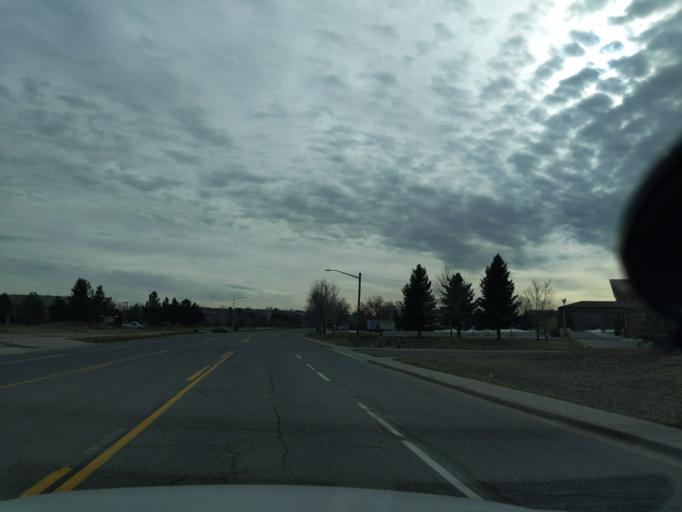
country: US
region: Colorado
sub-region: Adams County
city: Thornton
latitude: 39.8887
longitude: -104.9634
